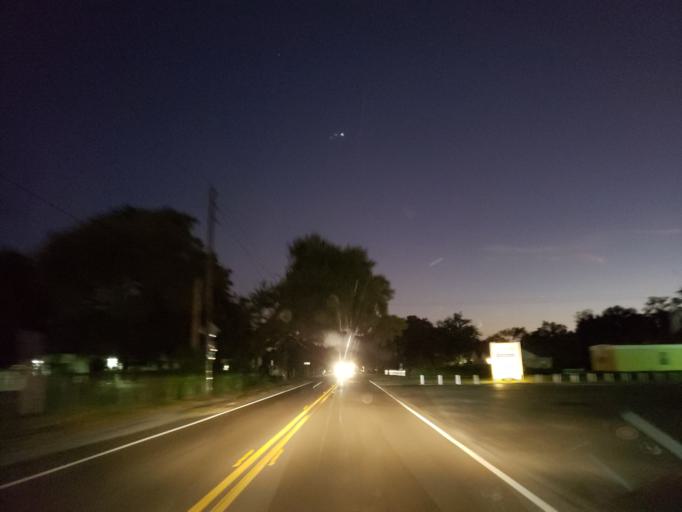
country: US
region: Florida
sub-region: Hillsborough County
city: Dover
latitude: 27.9934
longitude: -82.2197
